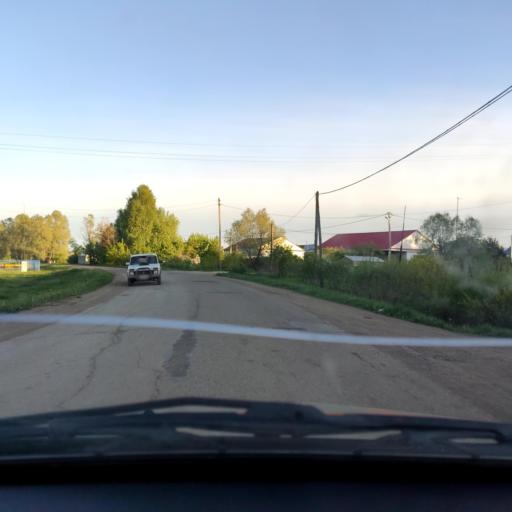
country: RU
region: Bashkortostan
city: Yazykovo
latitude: 55.0407
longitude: 56.1897
